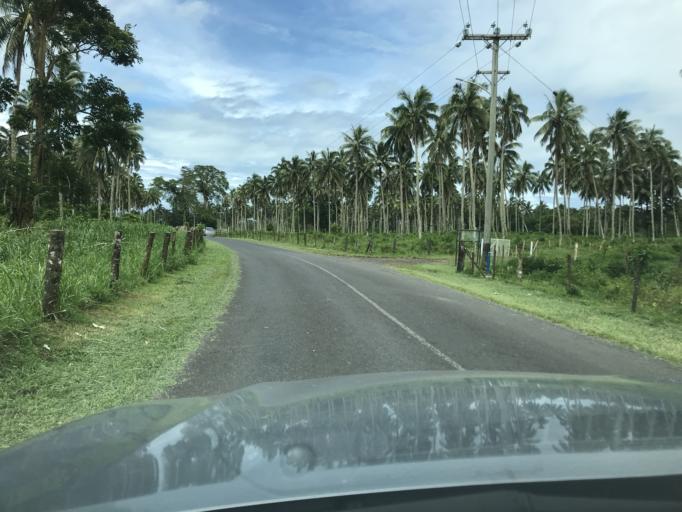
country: WS
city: Fasito`outa
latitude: -13.8724
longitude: -171.9152
